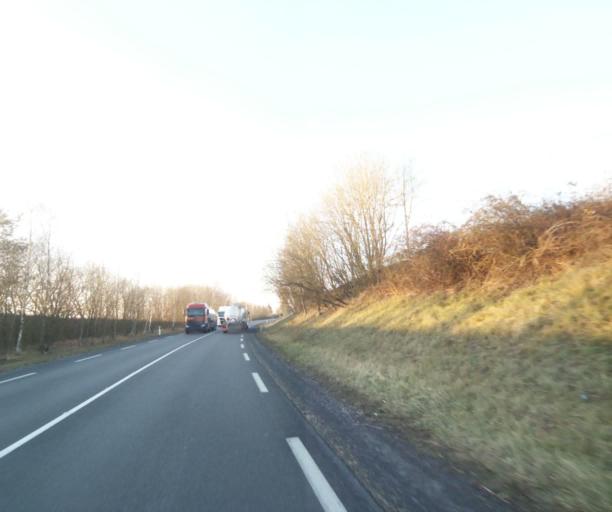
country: FR
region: Champagne-Ardenne
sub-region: Departement de la Haute-Marne
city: Bienville
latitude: 48.5467
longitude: 5.0686
